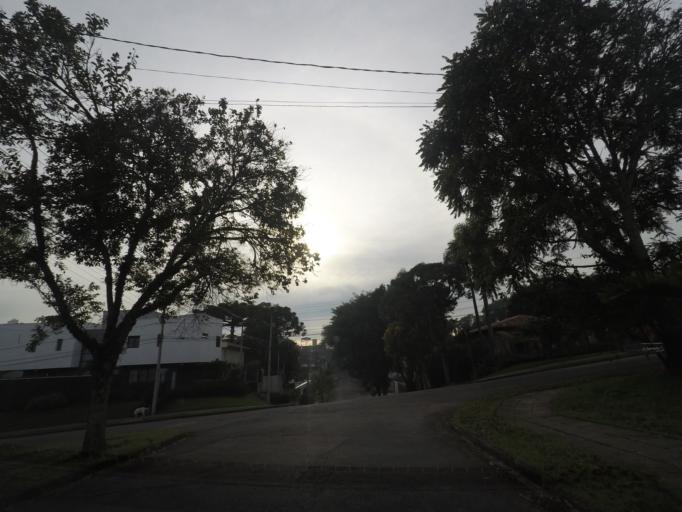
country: BR
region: Parana
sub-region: Curitiba
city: Curitiba
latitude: -25.4383
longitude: -49.3006
